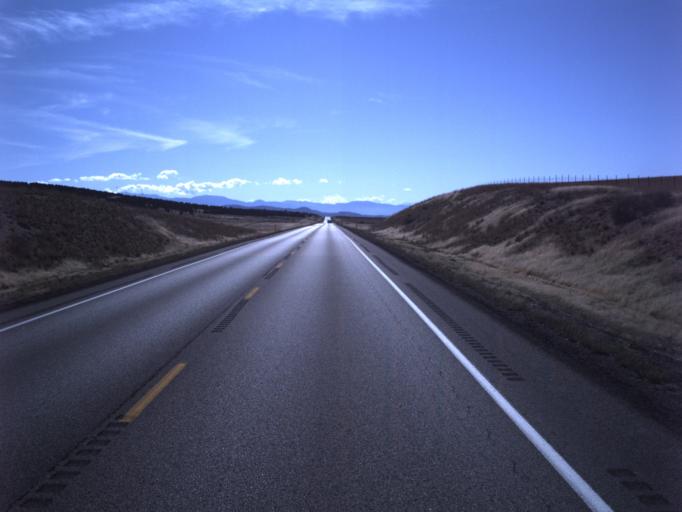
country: US
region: Utah
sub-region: Sanpete County
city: Gunnison
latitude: 39.3365
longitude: -111.9187
